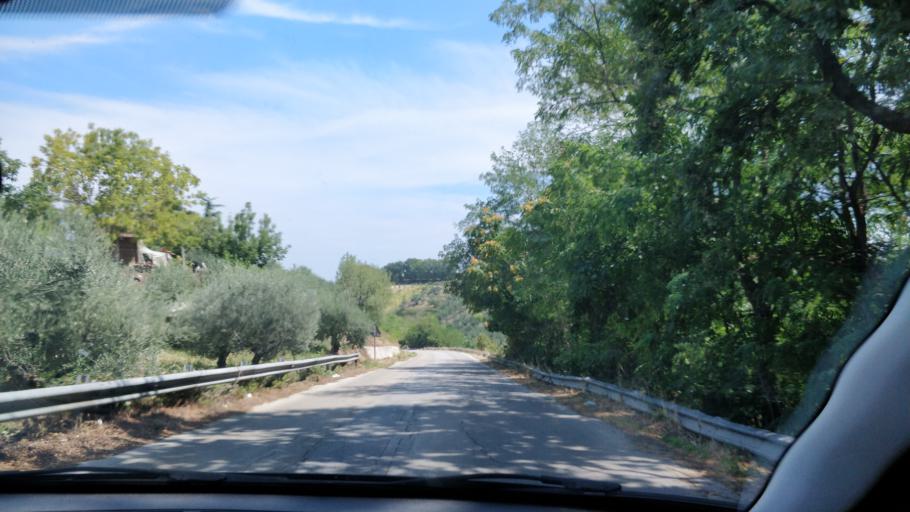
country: IT
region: Abruzzo
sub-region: Provincia di Chieti
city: Torrevecchia
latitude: 42.3981
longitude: 14.2023
